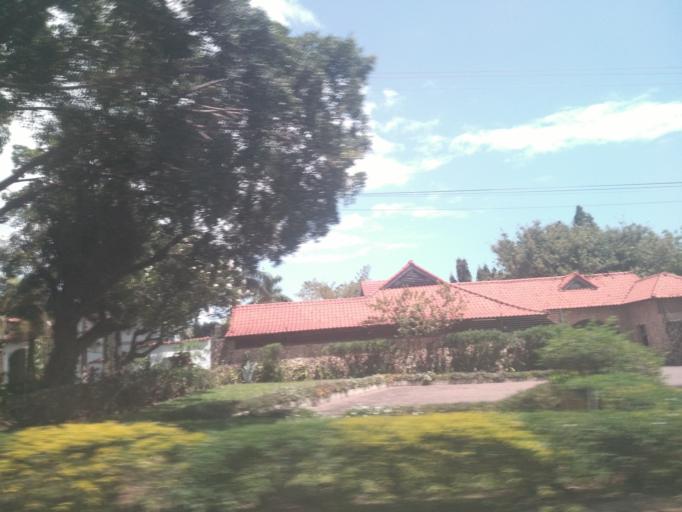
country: TZ
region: Dar es Salaam
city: Magomeni
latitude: -6.7410
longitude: 39.2780
